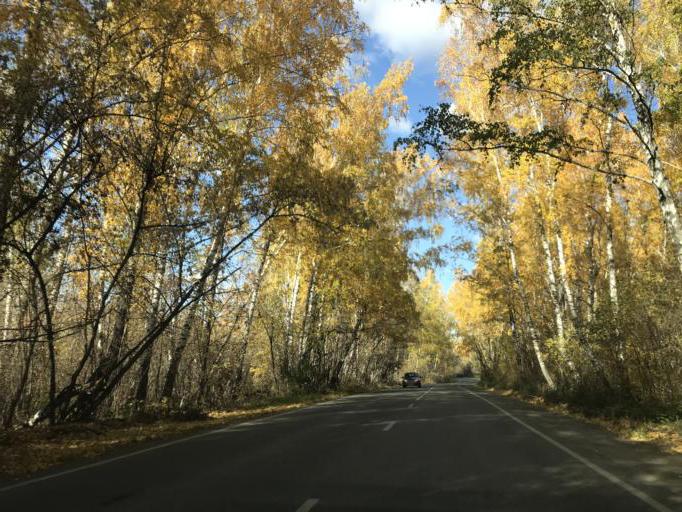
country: RU
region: Chelyabinsk
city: Dolgoderevenskoye
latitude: 55.2607
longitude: 61.3638
